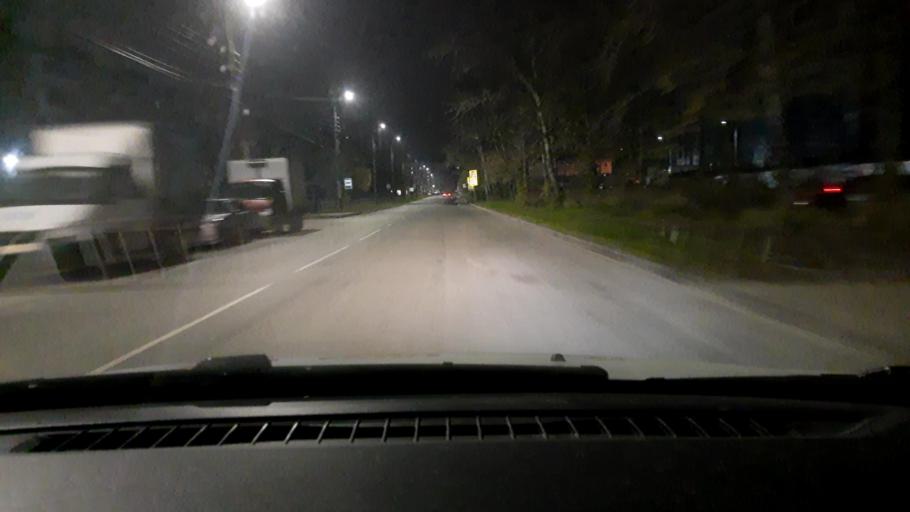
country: RU
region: Nizjnij Novgorod
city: Dzerzhinsk
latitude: 56.2561
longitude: 43.4611
